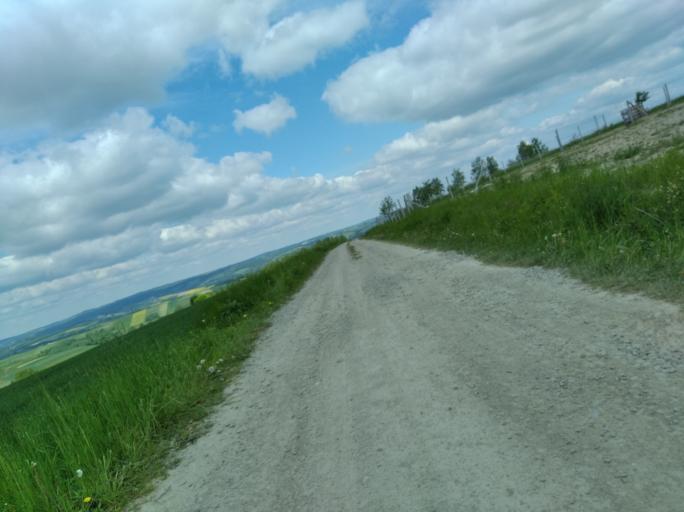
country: PL
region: Subcarpathian Voivodeship
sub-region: Powiat ropczycko-sedziszowski
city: Wielopole Skrzynskie
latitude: 49.8985
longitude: 21.5789
